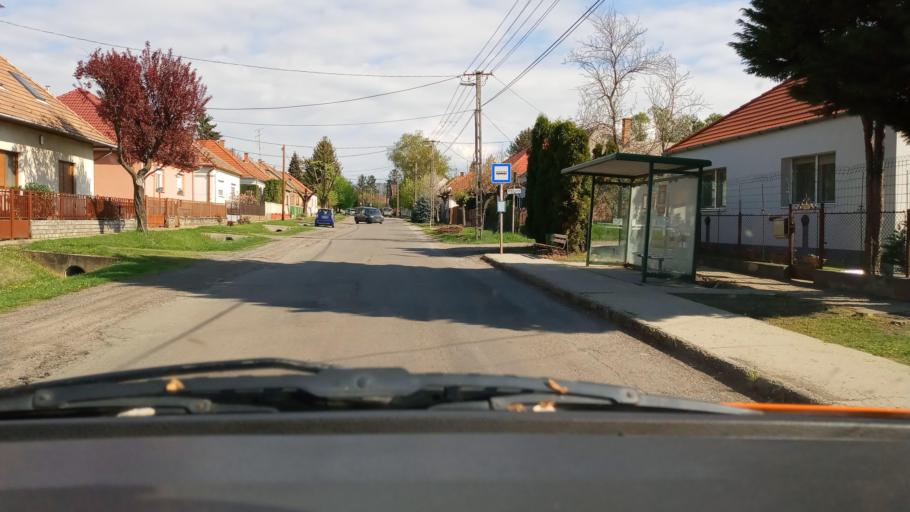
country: HU
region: Baranya
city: Hosszuheteny
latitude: 46.1155
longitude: 18.3410
